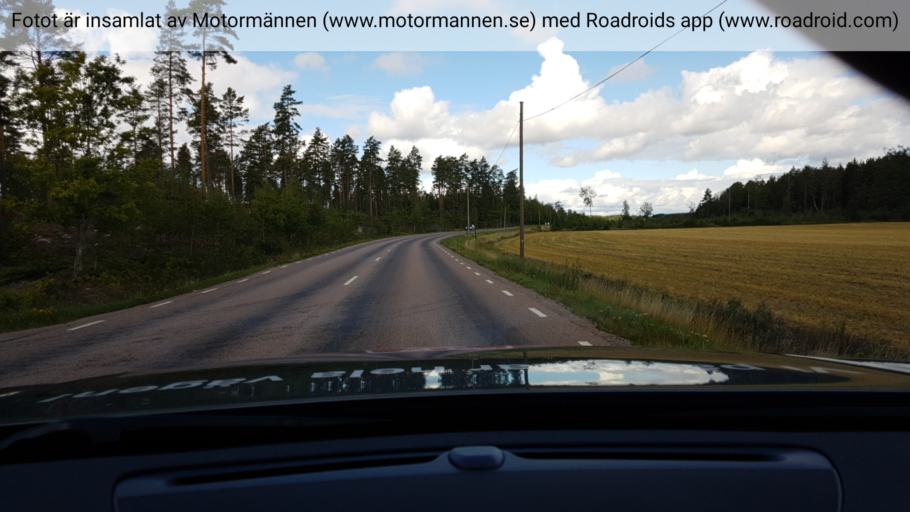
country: SE
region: Soedermanland
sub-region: Strangnas Kommun
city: Mariefred
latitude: 59.2977
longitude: 17.2200
